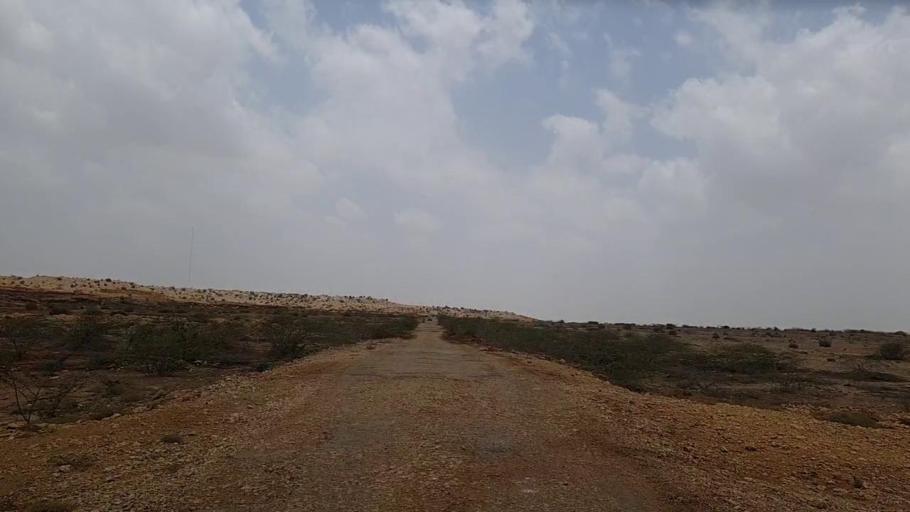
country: PK
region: Sindh
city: Thatta
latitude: 24.8893
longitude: 67.8965
